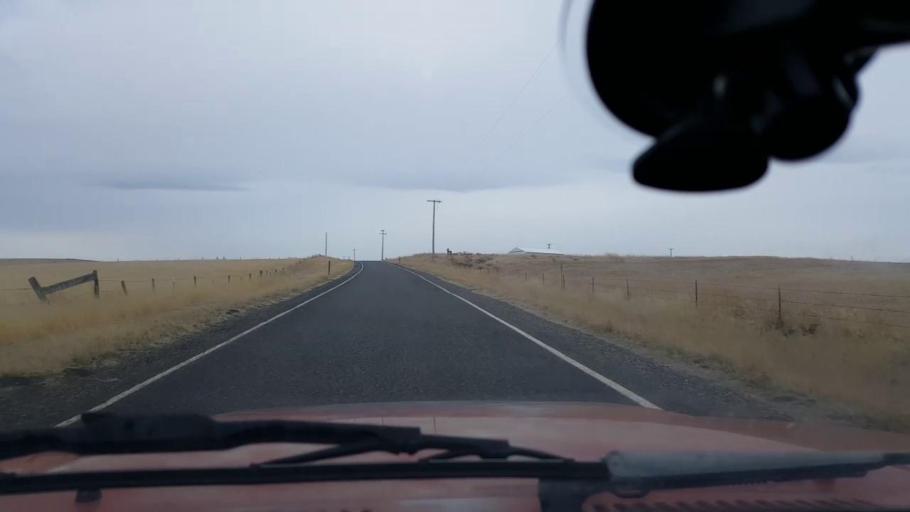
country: US
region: Washington
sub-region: Asotin County
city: Clarkston Heights-Vineland
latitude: 46.3257
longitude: -117.3252
